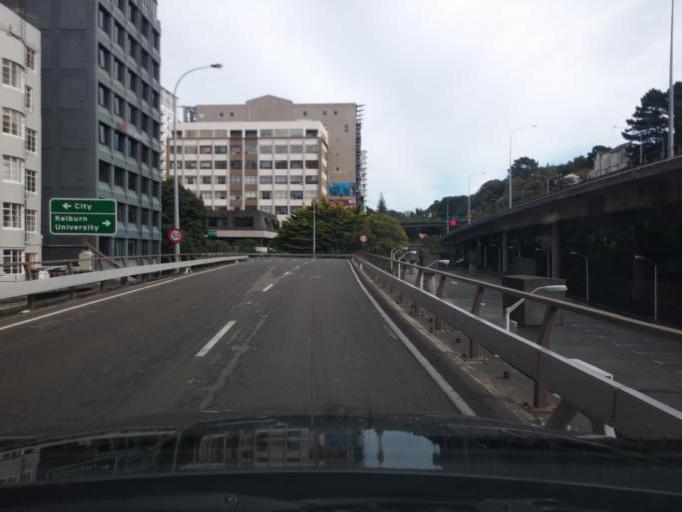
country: NZ
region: Wellington
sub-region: Wellington City
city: Wellington
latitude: -41.2834
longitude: 174.7740
